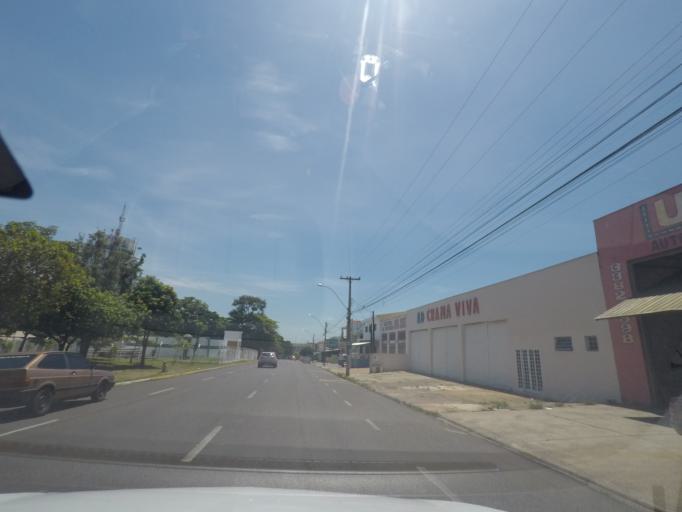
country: BR
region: Sao Paulo
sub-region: Matao
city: Matao
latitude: -21.6156
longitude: -48.3541
